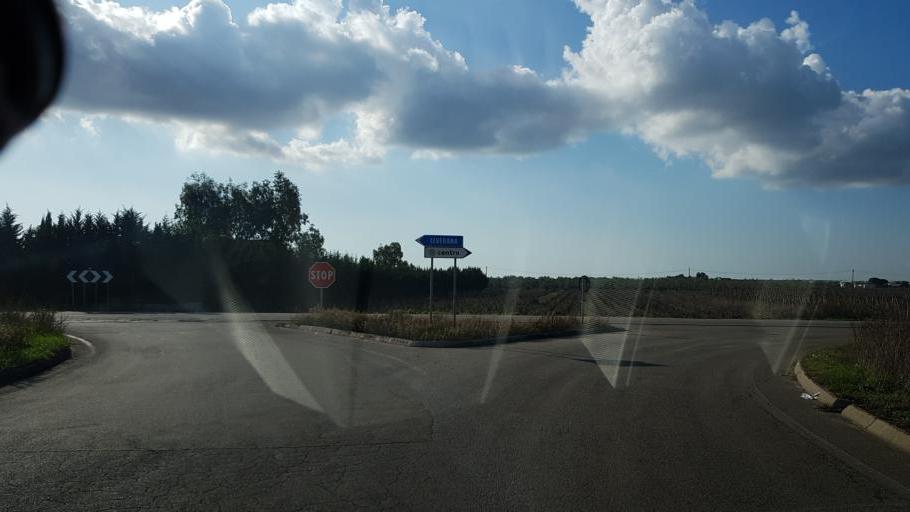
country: IT
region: Apulia
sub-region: Provincia di Lecce
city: Veglie
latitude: 40.3237
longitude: 17.9776
